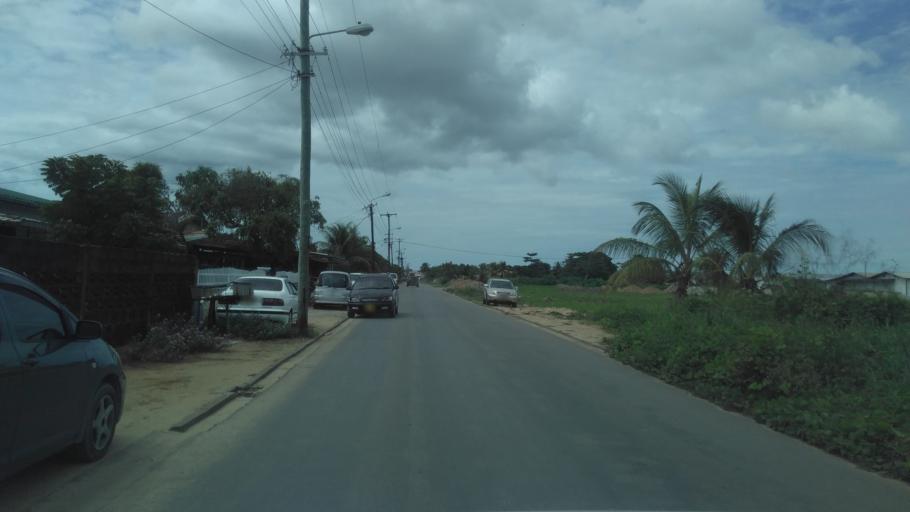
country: SR
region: Paramaribo
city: Paramaribo
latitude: 5.8472
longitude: -55.1242
